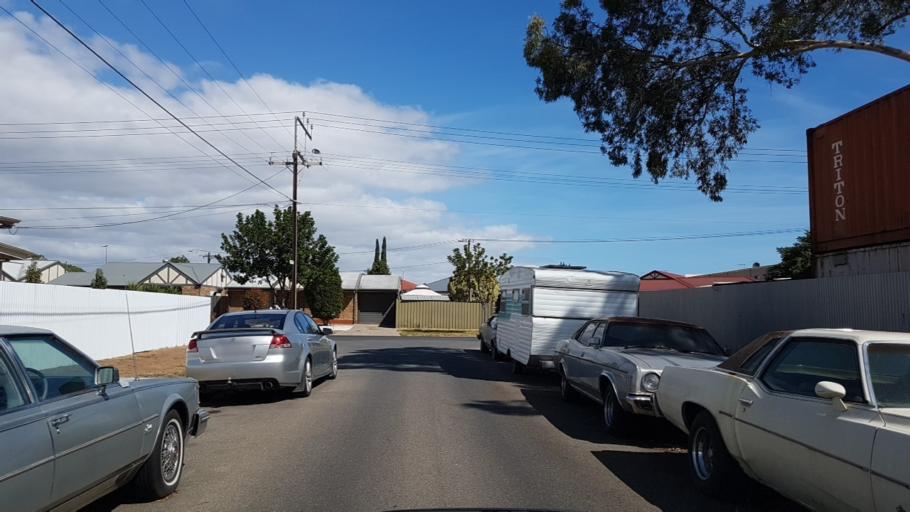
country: AU
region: South Australia
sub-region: Charles Sturt
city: Woodville North
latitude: -34.8553
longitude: 138.5427
